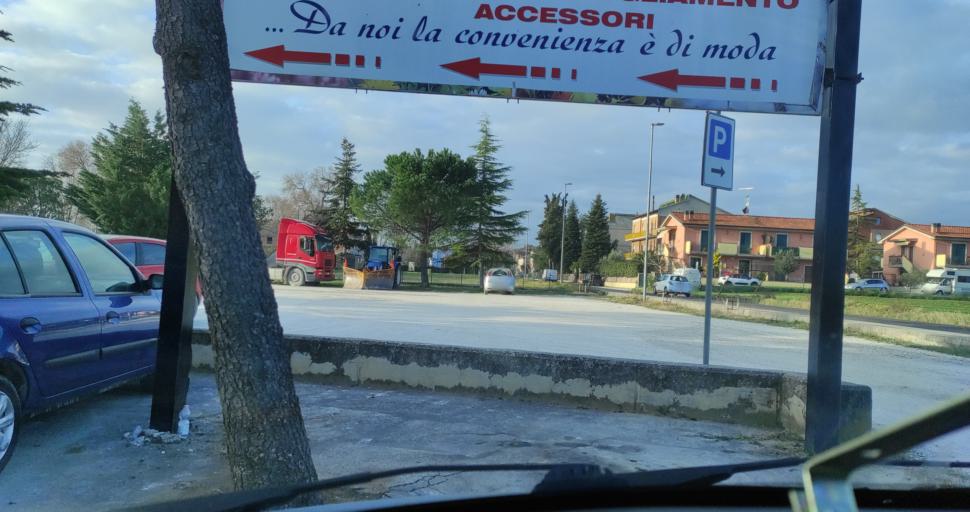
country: IT
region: The Marches
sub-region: Provincia di Macerata
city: Urbisaglia
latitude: 43.2081
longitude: 13.3912
